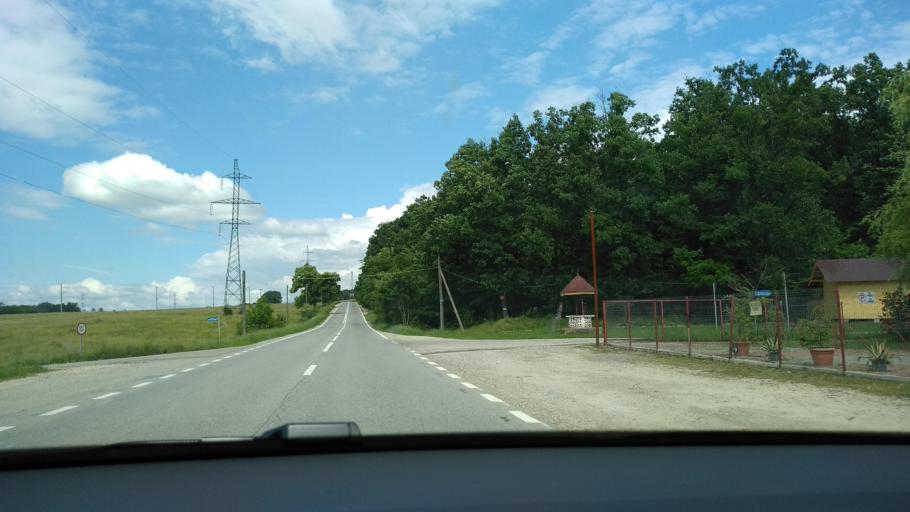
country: RO
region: Valcea
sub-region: Comuna Slatioara
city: Slatioara
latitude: 45.1286
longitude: 23.8685
